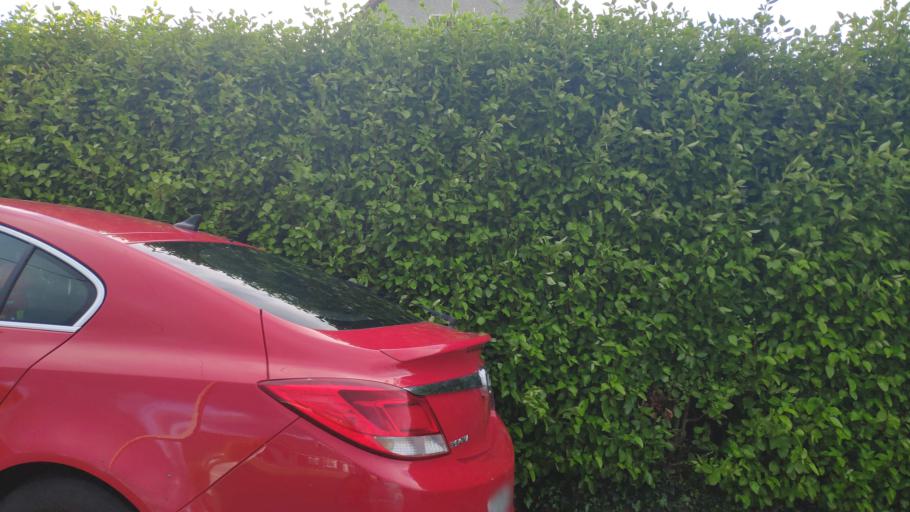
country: IE
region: Munster
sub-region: County Cork
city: Cork
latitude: 51.9088
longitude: -8.4847
